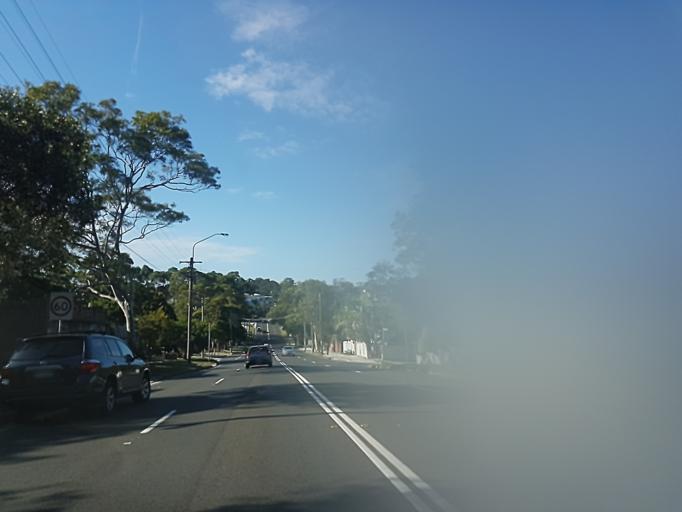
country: AU
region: New South Wales
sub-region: North Sydney
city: Cammeray
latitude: -33.8076
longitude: 151.2084
